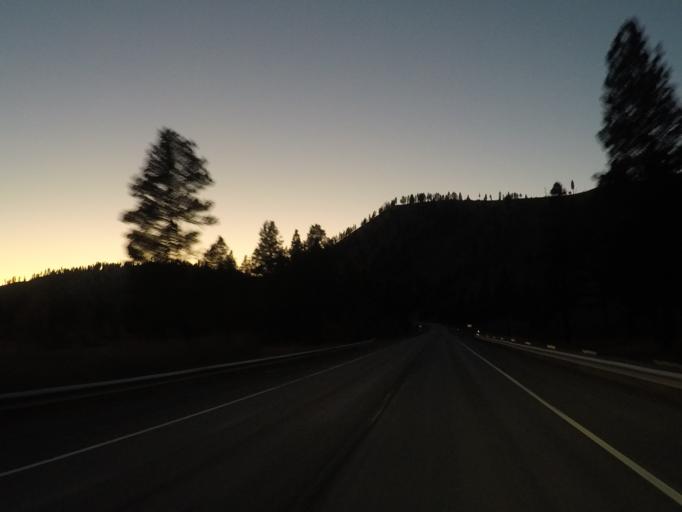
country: US
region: Montana
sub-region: Missoula County
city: Seeley Lake
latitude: 47.0238
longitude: -113.3004
